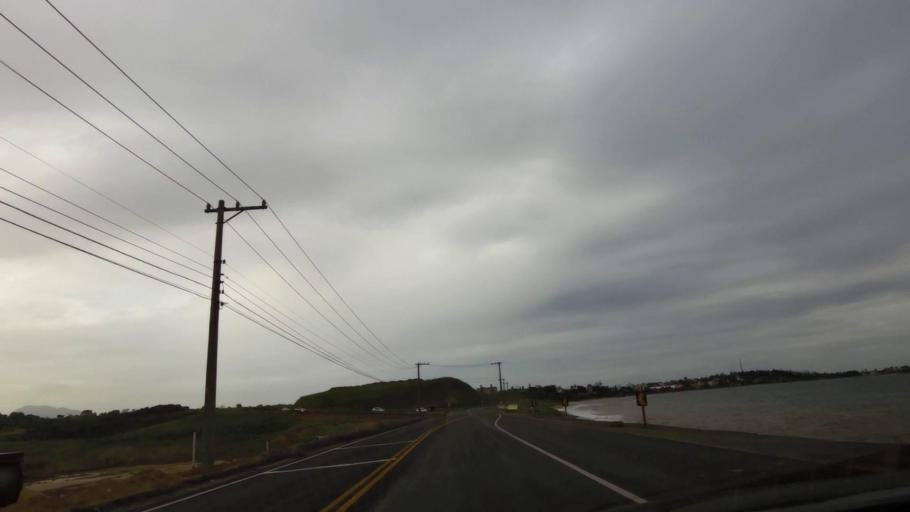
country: BR
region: Espirito Santo
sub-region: Guarapari
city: Guarapari
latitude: -20.7429
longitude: -40.5532
